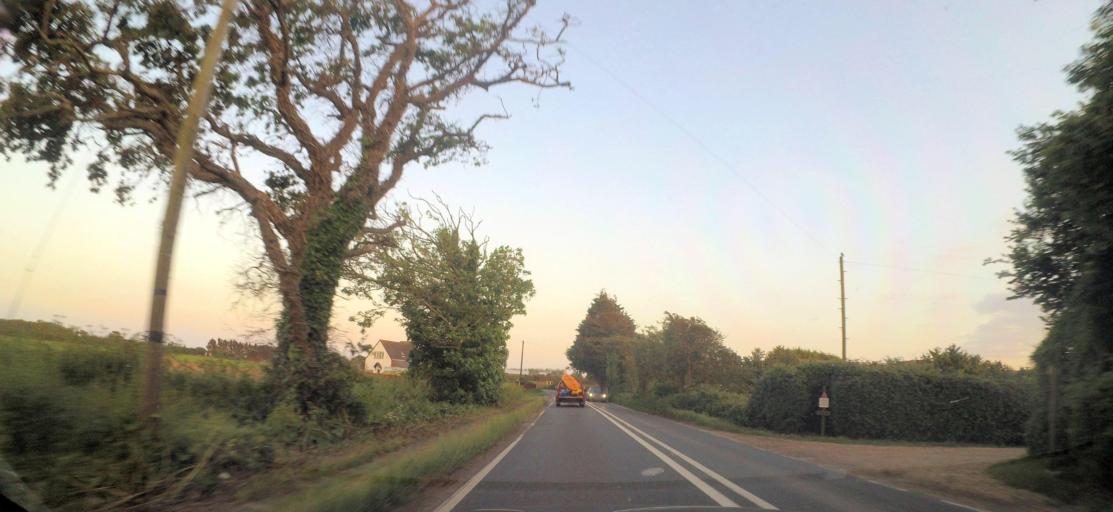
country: GB
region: England
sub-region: West Sussex
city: Selsey
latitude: 50.7478
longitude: -0.7814
